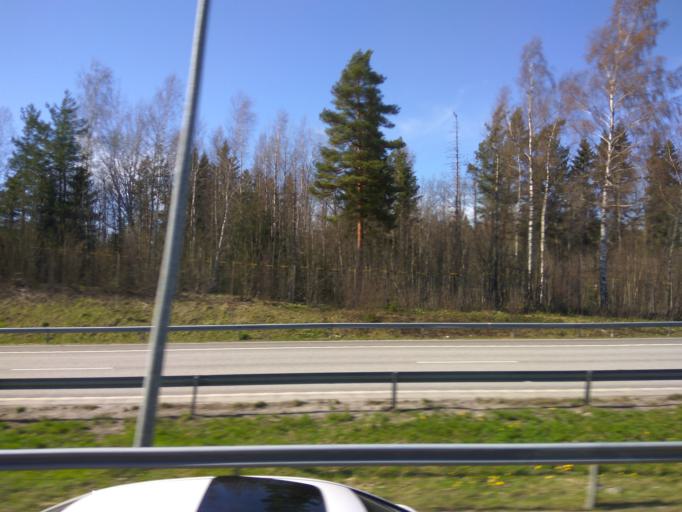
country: FI
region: Uusimaa
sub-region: Helsinki
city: Nickby
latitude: 60.3063
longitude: 25.3788
